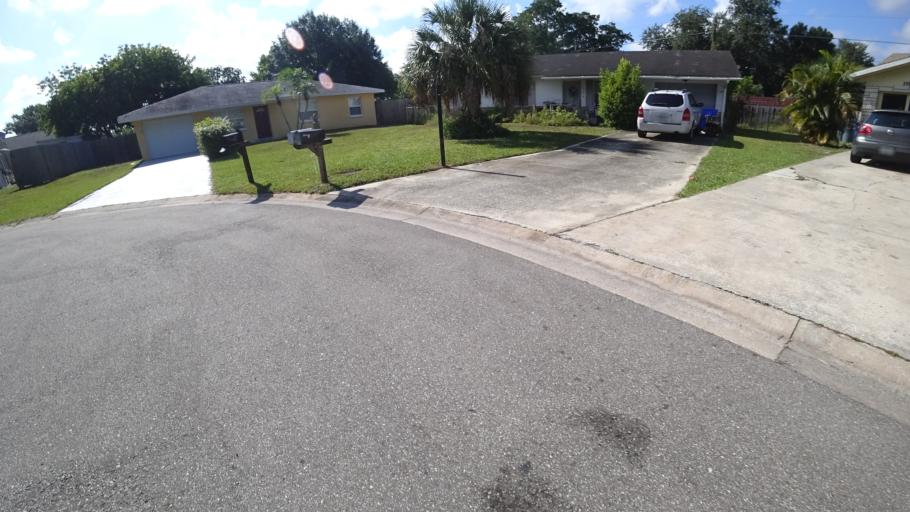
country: US
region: Florida
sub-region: Manatee County
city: Ellenton
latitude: 27.4968
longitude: -82.4777
